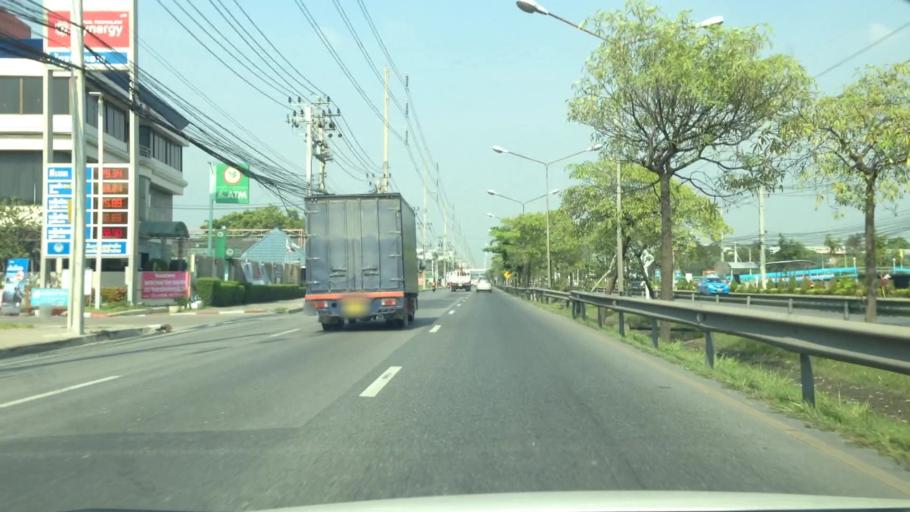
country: TH
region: Samut Prakan
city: Samut Prakan
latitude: 13.5277
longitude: 100.6367
